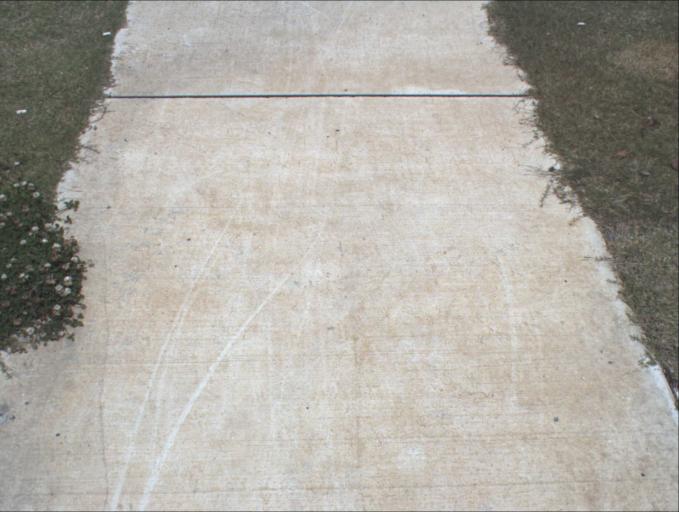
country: AU
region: Queensland
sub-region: Logan
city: Chambers Flat
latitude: -27.8073
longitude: 153.1114
